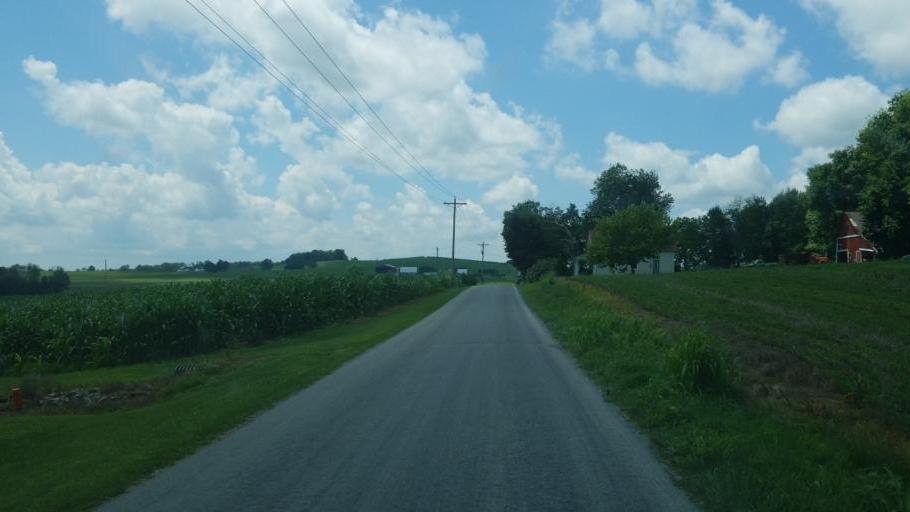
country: US
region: Ohio
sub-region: Highland County
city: Greenfield
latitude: 39.2426
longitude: -83.4486
